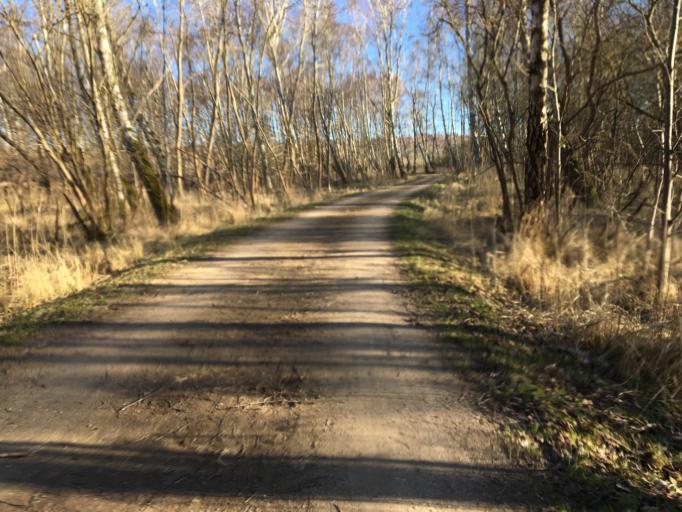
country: DK
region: Capital Region
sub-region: Tarnby Kommune
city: Tarnby
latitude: 55.5939
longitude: 12.5554
